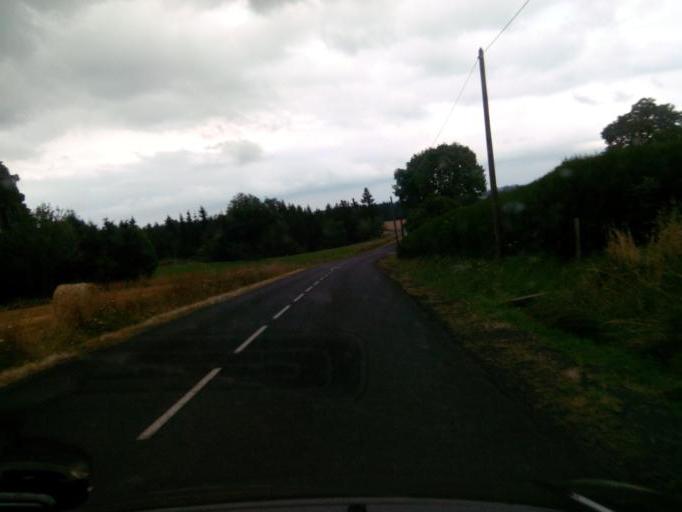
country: FR
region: Rhone-Alpes
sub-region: Departement de la Loire
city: Usson-en-Forez
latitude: 45.3551
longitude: 3.9750
